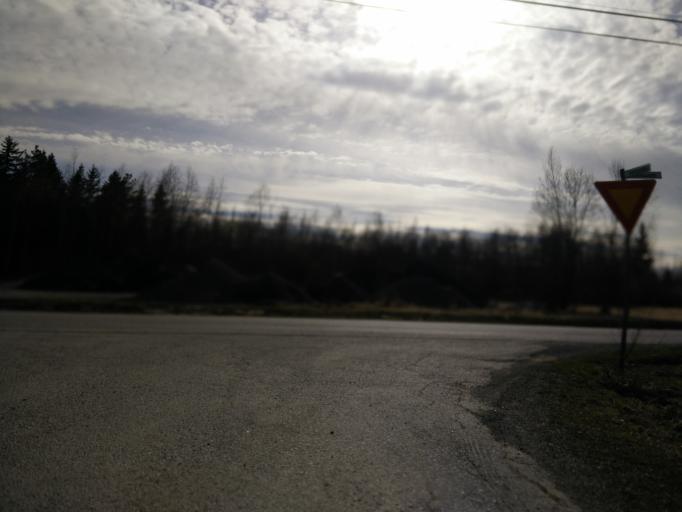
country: FI
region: Pirkanmaa
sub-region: Tampere
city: Orivesi
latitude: 61.6932
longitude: 24.3634
